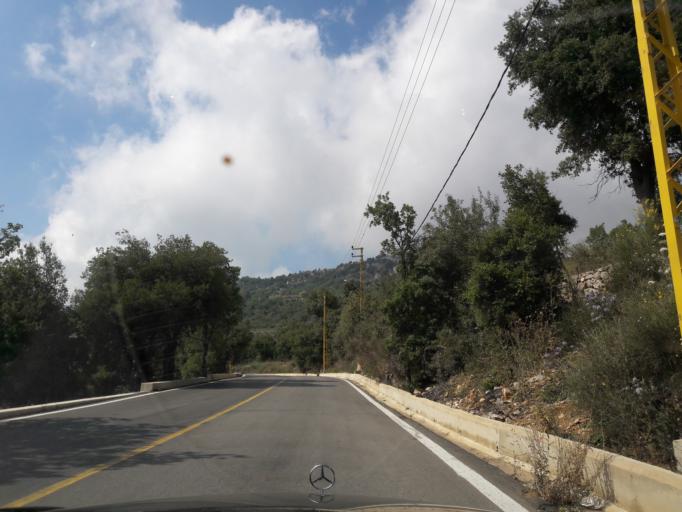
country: LB
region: Mont-Liban
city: Djounie
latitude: 33.9636
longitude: 35.7743
